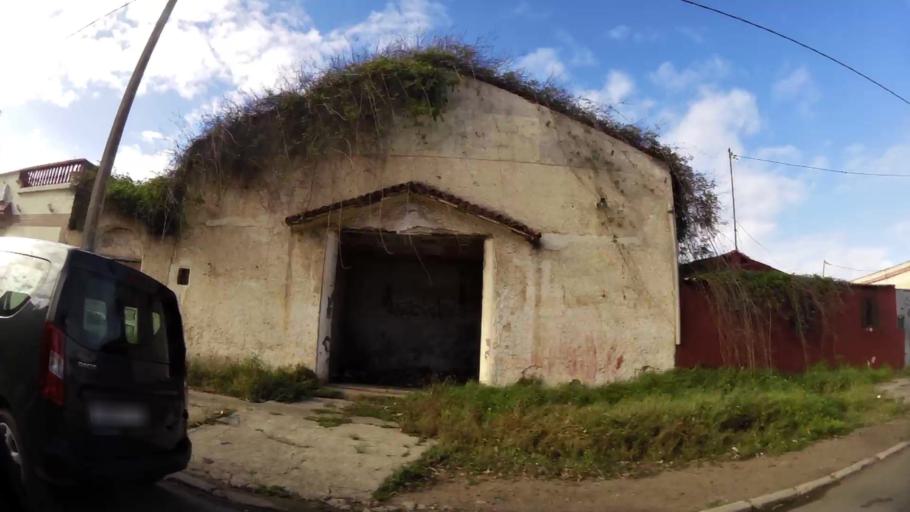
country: MA
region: Grand Casablanca
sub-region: Mohammedia
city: Mohammedia
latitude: 33.7087
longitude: -7.4010
